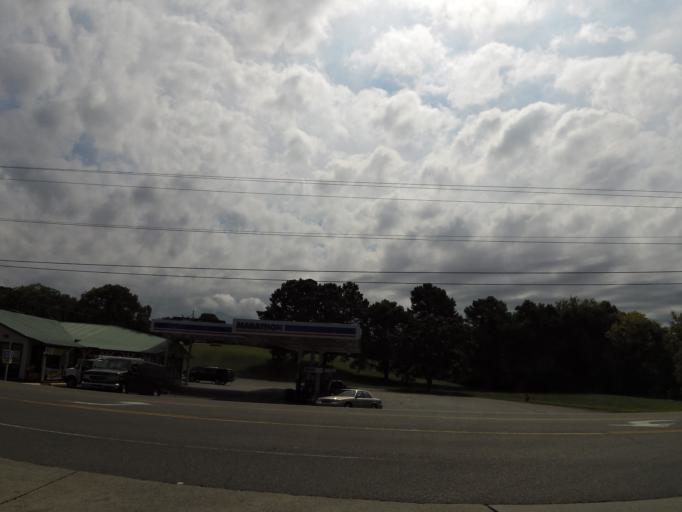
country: US
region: Tennessee
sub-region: Humphreys County
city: Waverly
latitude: 35.8819
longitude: -87.8005
